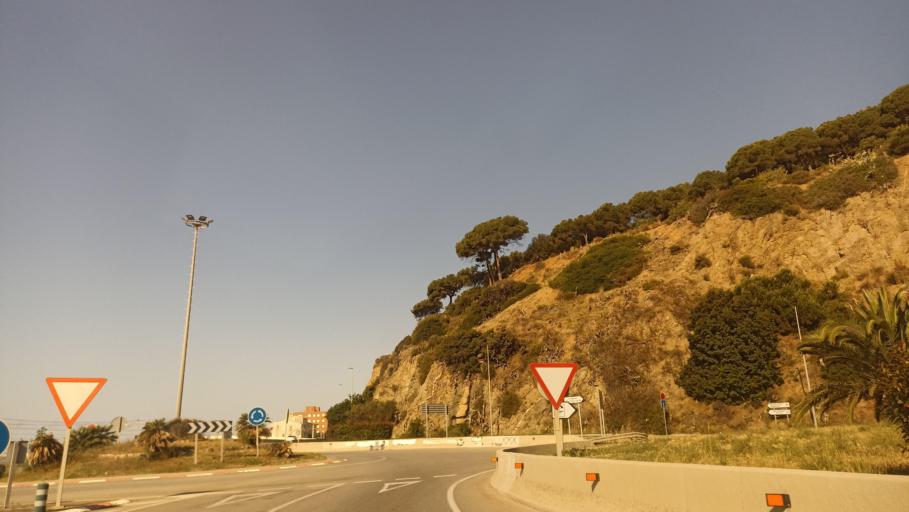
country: ES
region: Catalonia
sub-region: Provincia de Barcelona
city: Caldes d'Estrac
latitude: 41.5726
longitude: 2.5357
